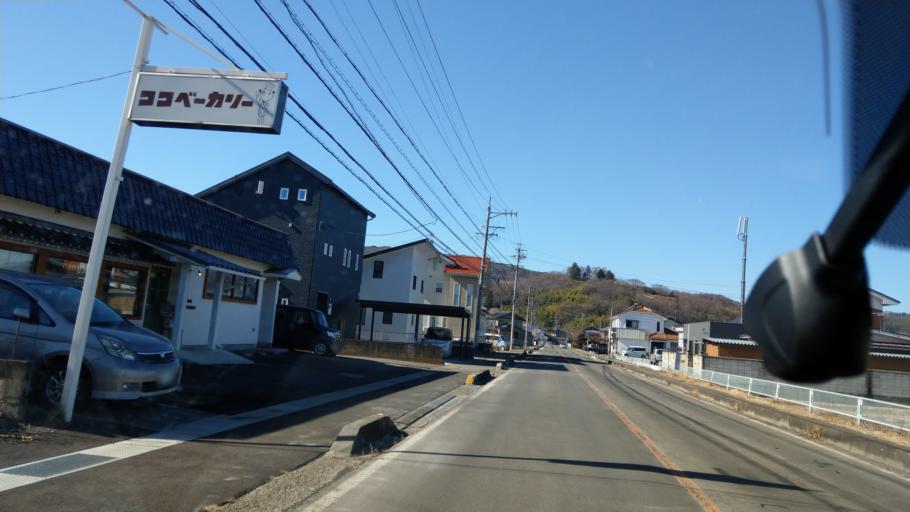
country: JP
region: Nagano
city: Saku
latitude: 36.2253
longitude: 138.4493
